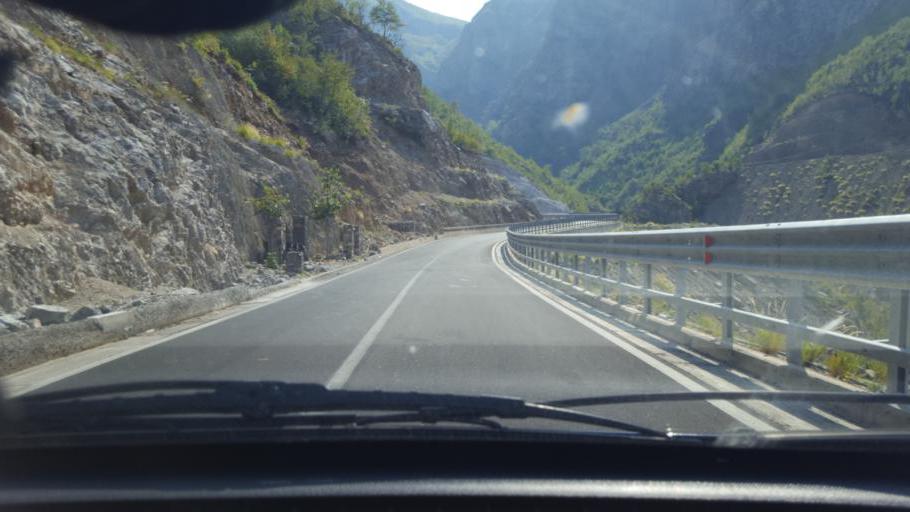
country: AL
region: Shkoder
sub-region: Rrethi i Malesia e Madhe
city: Kastrat
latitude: 42.4154
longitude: 19.5111
